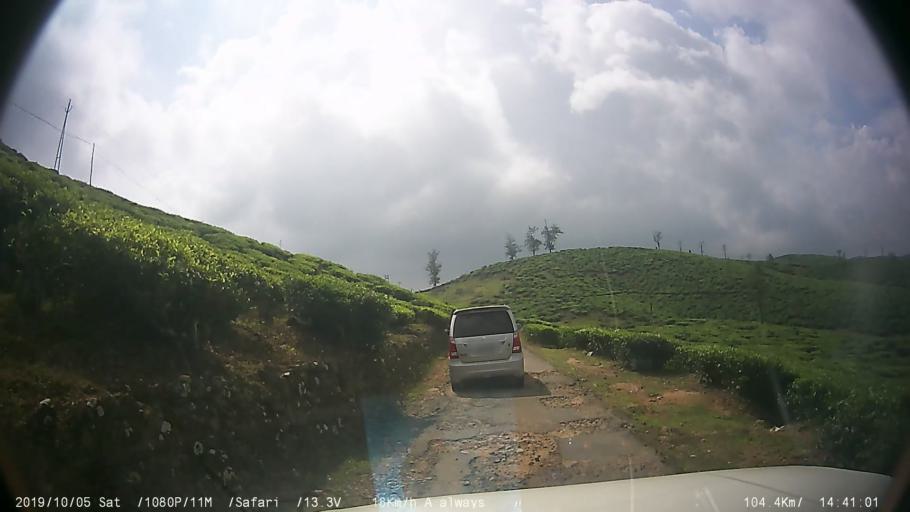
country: IN
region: Kerala
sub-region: Kottayam
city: Erattupetta
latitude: 9.6201
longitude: 76.9511
